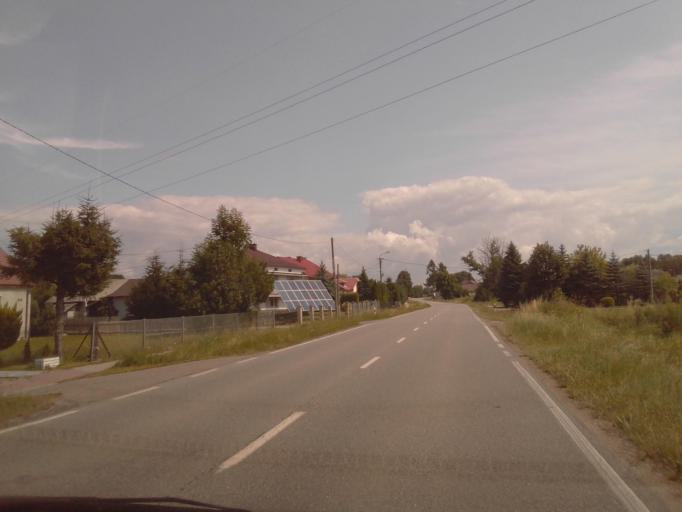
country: PL
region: Subcarpathian Voivodeship
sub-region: Powiat ropczycko-sedziszowski
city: Ropczyce
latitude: 50.0442
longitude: 21.5913
